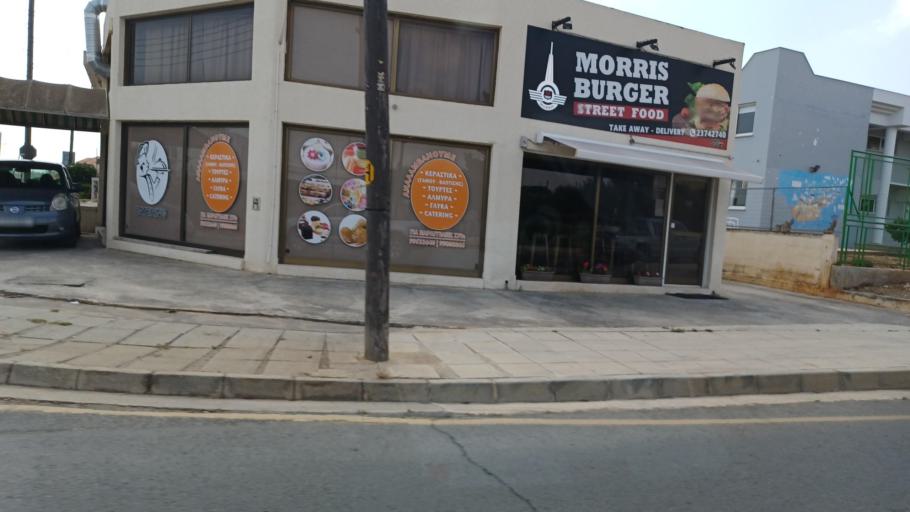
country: CY
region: Ammochostos
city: Deryneia
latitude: 35.0588
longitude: 33.9583
